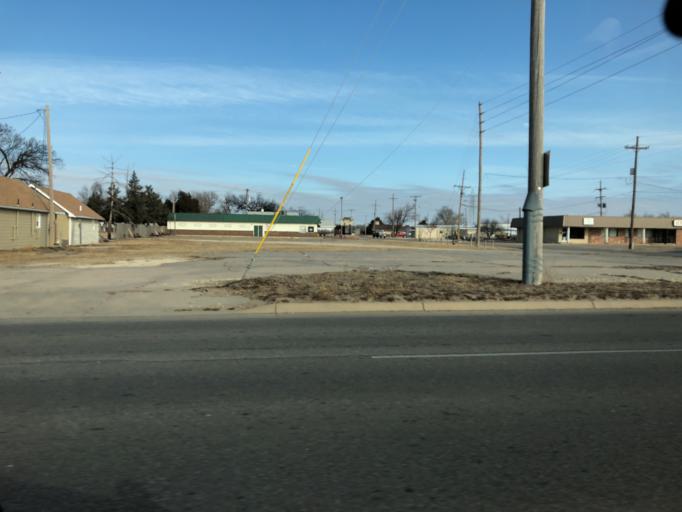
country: US
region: Kansas
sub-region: Reno County
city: Hutchinson
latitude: 38.0570
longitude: -97.9504
